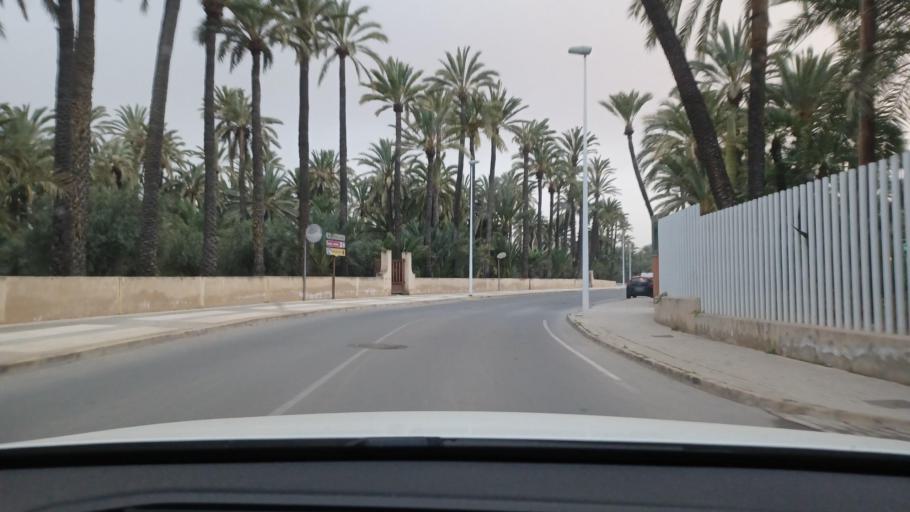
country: ES
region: Valencia
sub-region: Provincia de Alicante
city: Elche
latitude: 38.2589
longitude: -0.6932
